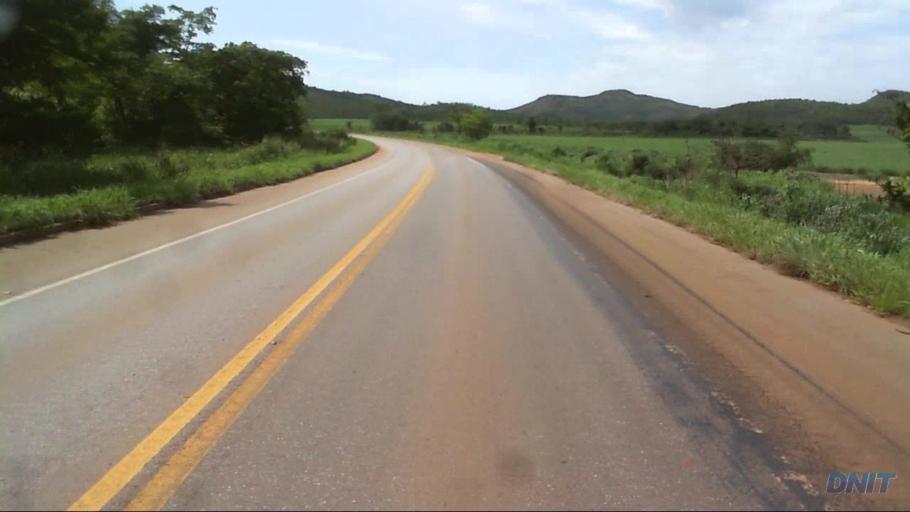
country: BR
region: Goias
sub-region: Barro Alto
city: Barro Alto
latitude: -15.1288
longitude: -48.8351
